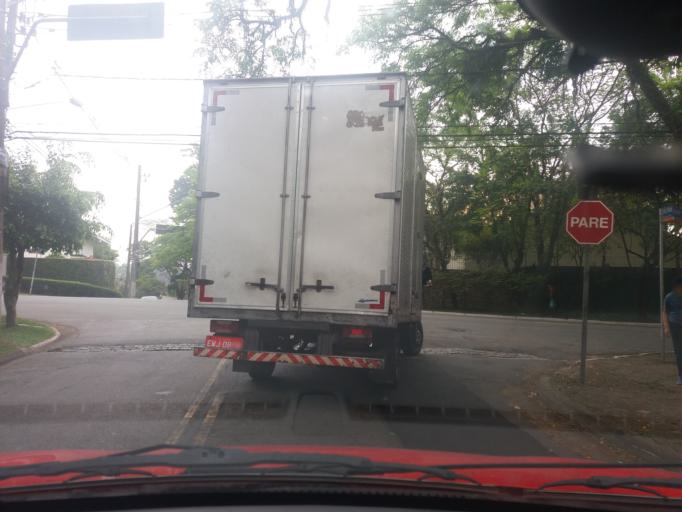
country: BR
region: Sao Paulo
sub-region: Sao Paulo
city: Sao Paulo
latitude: -23.5921
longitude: -46.7112
